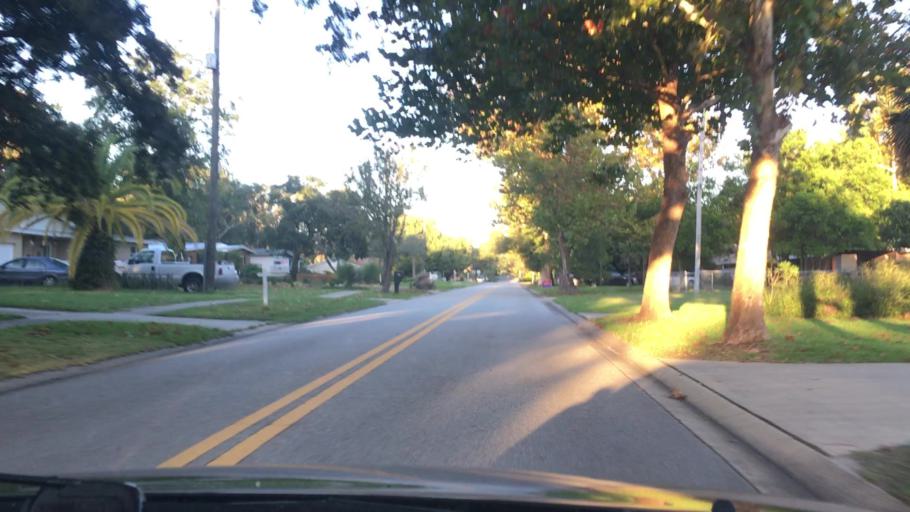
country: US
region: Florida
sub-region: Volusia County
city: Ormond Beach
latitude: 29.2931
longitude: -81.0672
